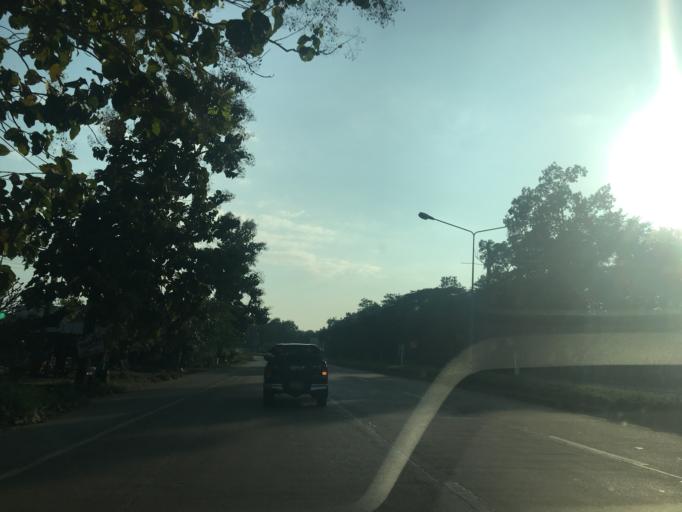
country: TH
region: Lampang
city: Ngao
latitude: 18.7342
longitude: 99.9718
